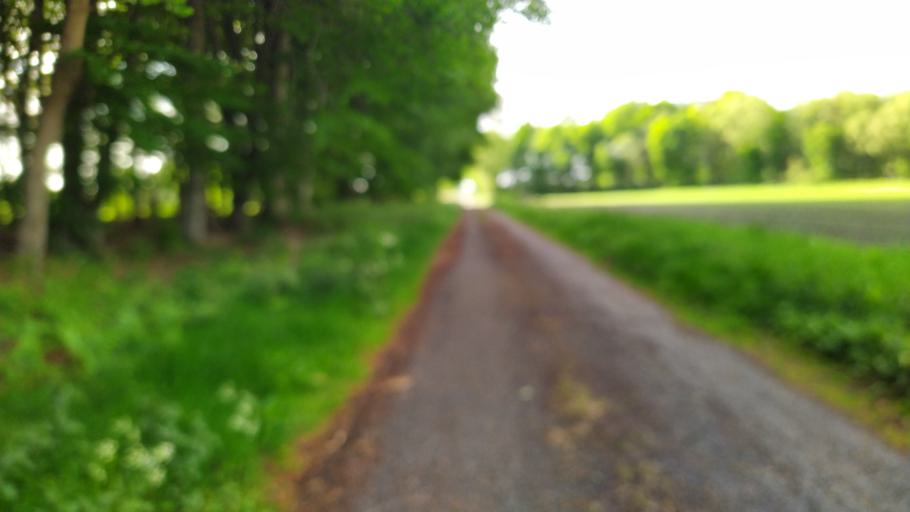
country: DE
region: Lower Saxony
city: Farven
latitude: 53.4440
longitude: 9.2830
